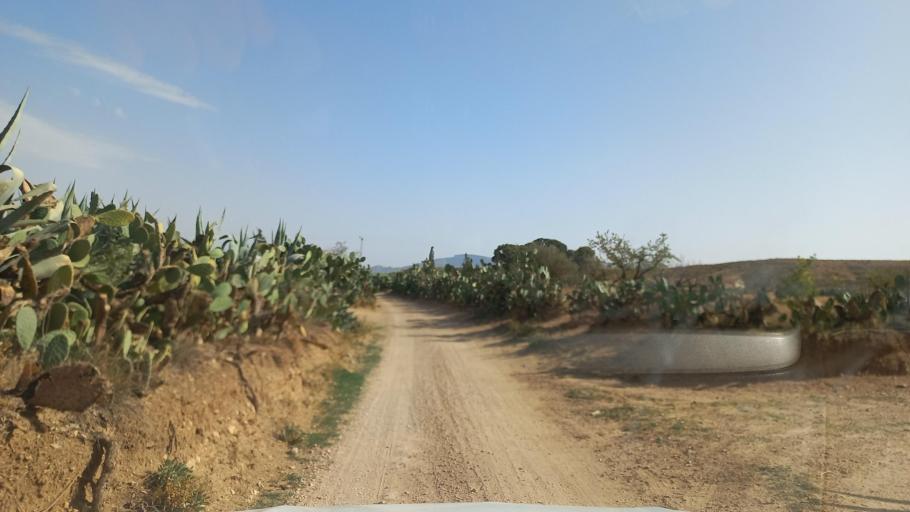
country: TN
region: Al Qasrayn
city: Kasserine
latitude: 35.2528
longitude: 8.9287
